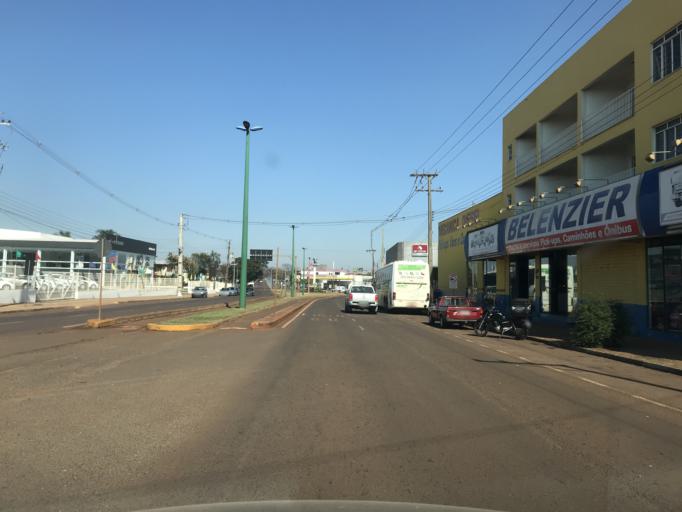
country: BR
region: Parana
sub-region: Toledo
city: Toledo
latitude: -24.7193
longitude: -53.7142
